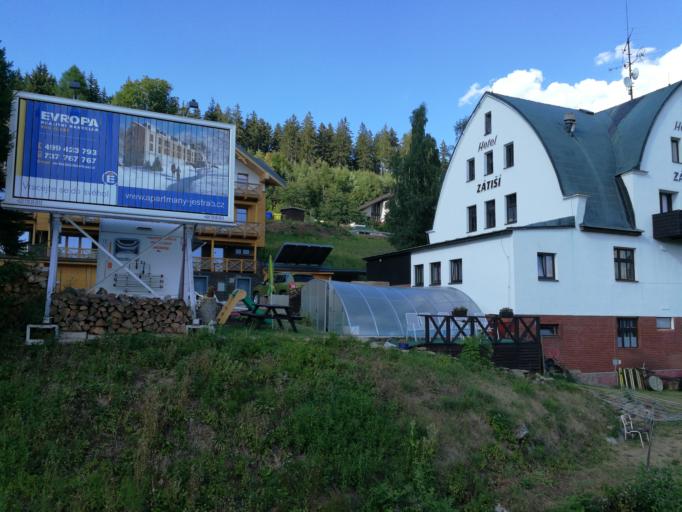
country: CZ
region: Kralovehradecky
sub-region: Okres Trutnov
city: Svoboda nad Upou
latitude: 50.6321
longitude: 15.7700
